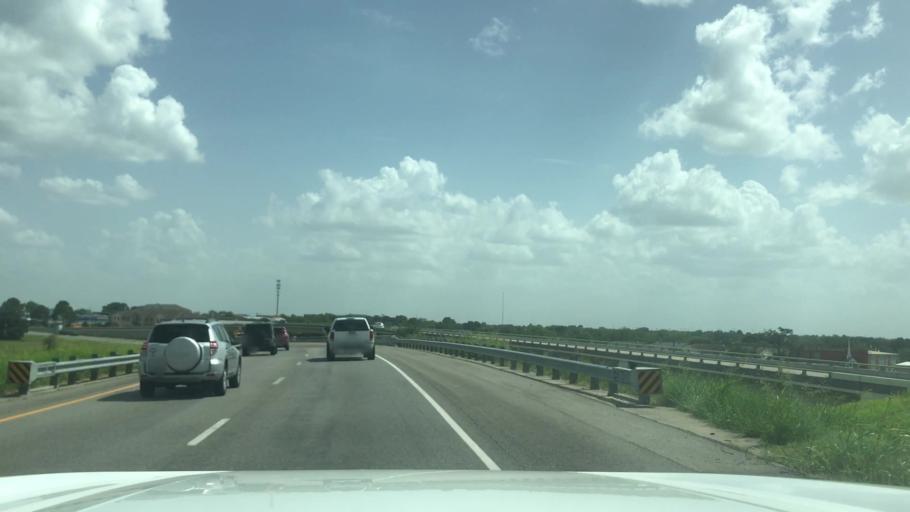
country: US
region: Texas
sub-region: Brazos County
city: College Station
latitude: 30.5937
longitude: -96.2906
